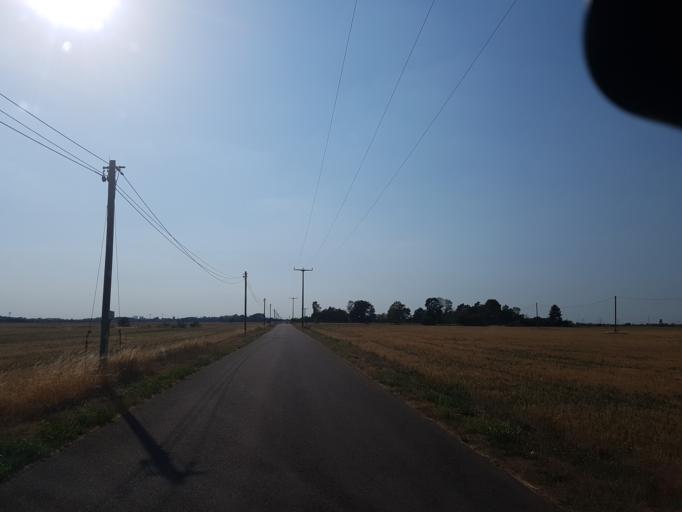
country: DE
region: Saxony
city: Beilrode
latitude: 51.5652
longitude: 13.1075
